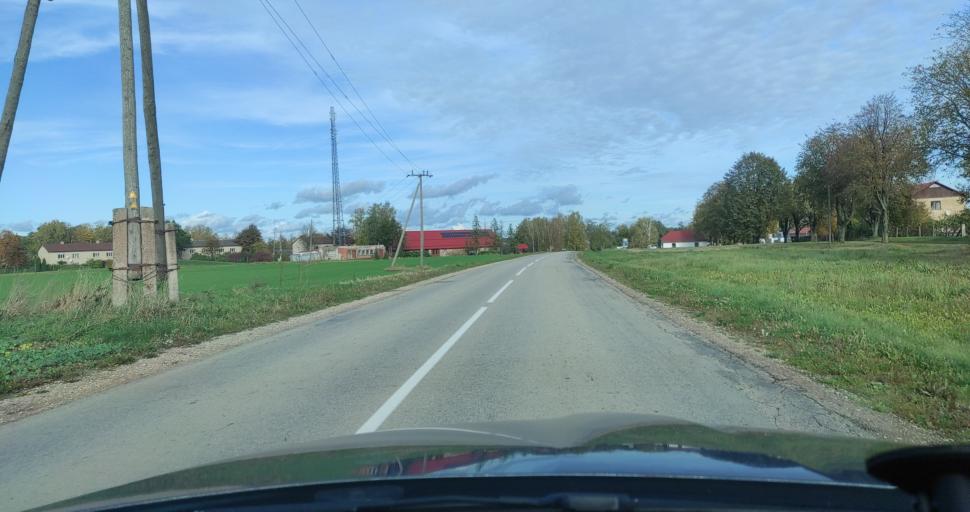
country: LV
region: Jaunpils
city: Jaunpils
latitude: 56.7273
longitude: 23.0092
